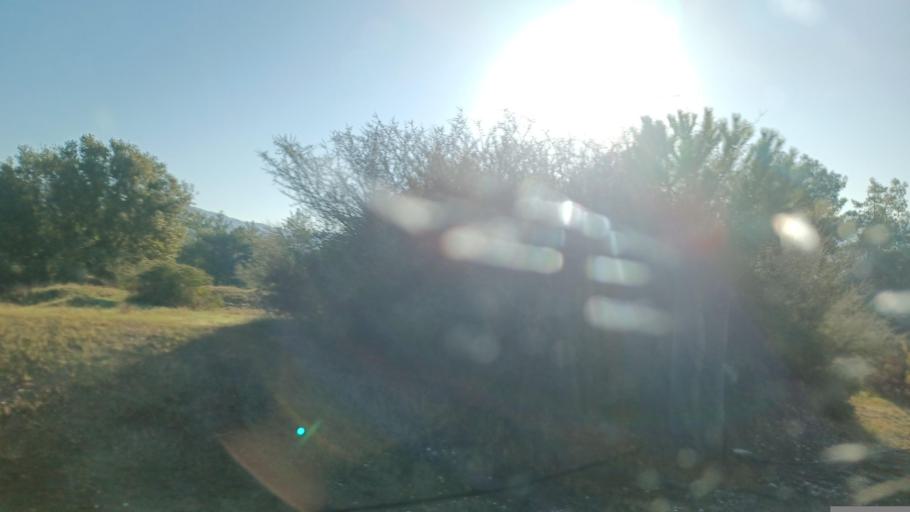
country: CY
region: Pafos
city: Mesogi
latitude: 34.9415
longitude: 32.5692
